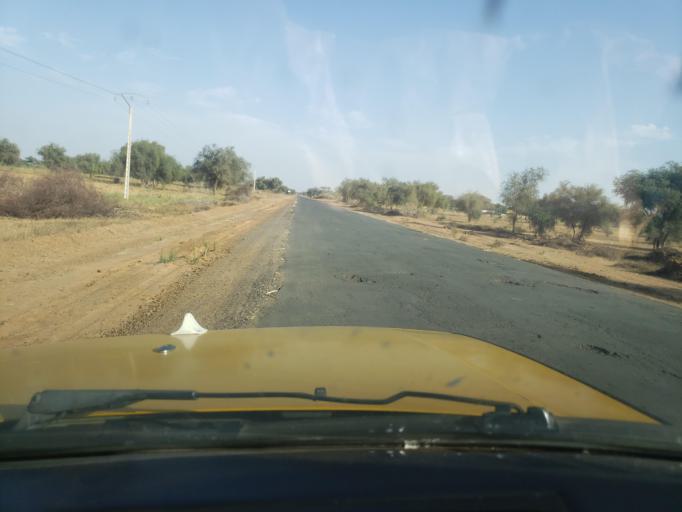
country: SN
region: Louga
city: Louga
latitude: 15.5024
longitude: -15.9451
